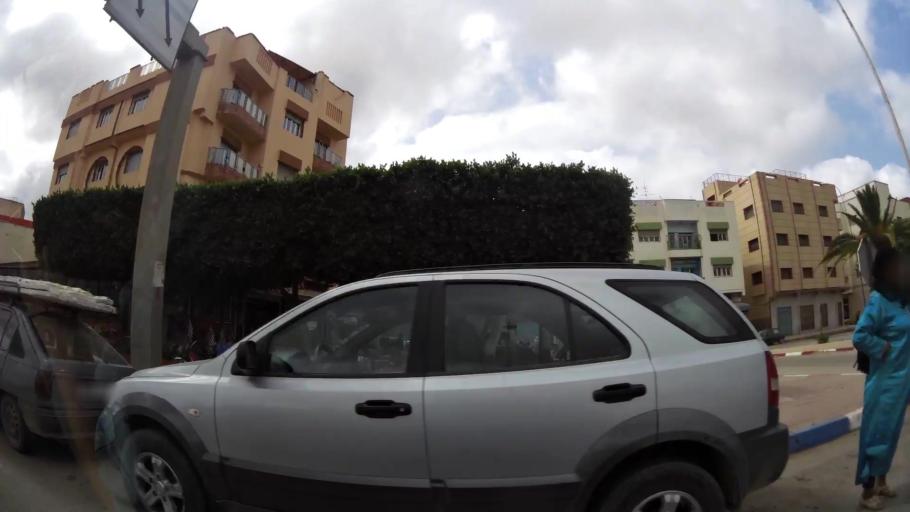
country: MA
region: Oriental
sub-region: Nador
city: Nador
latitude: 35.1755
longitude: -2.9331
